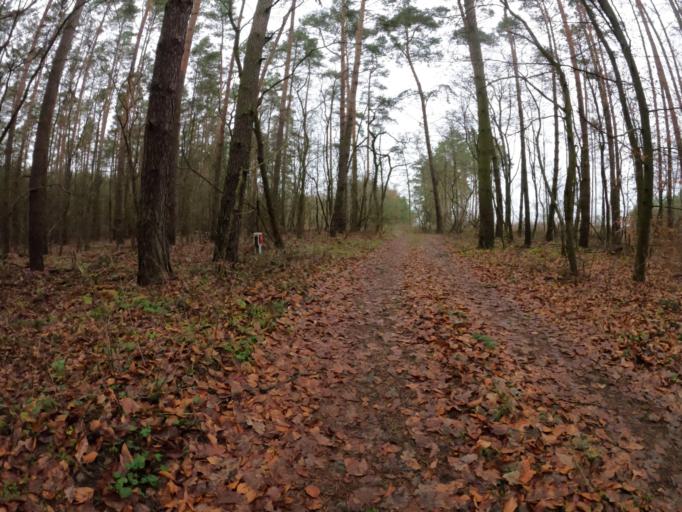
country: PL
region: West Pomeranian Voivodeship
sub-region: Powiat mysliborski
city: Debno
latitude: 52.7648
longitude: 14.7582
